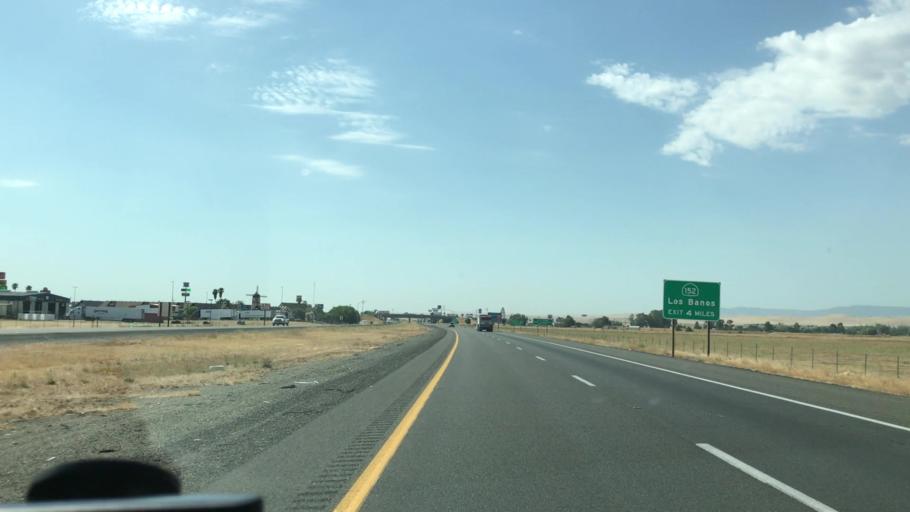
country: US
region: California
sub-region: Merced County
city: Gustine
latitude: 37.1134
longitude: -121.0216
